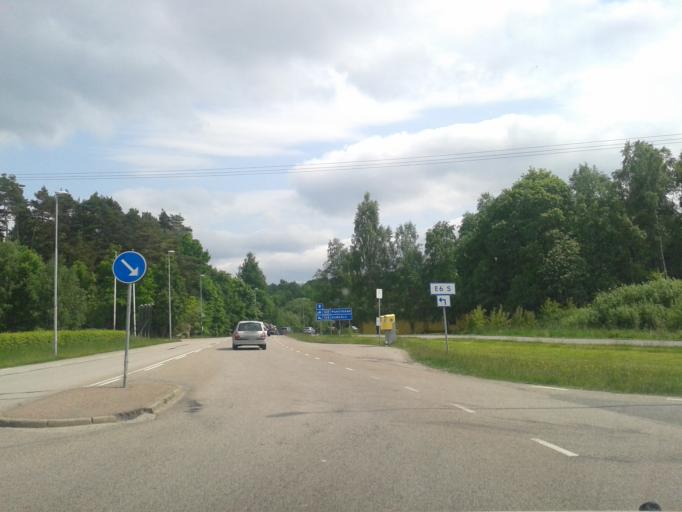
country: SE
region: Vaestra Goetaland
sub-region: Kungalvs Kommun
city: Kungalv
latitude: 57.8721
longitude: 11.9422
